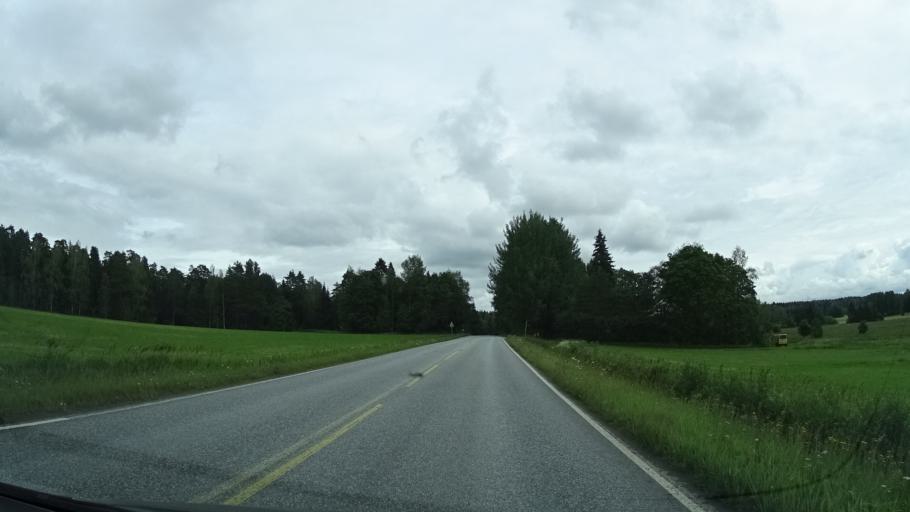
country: FI
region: Pirkanmaa
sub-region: Etelae-Pirkanmaa
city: Urjala
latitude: 61.0915
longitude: 23.4980
